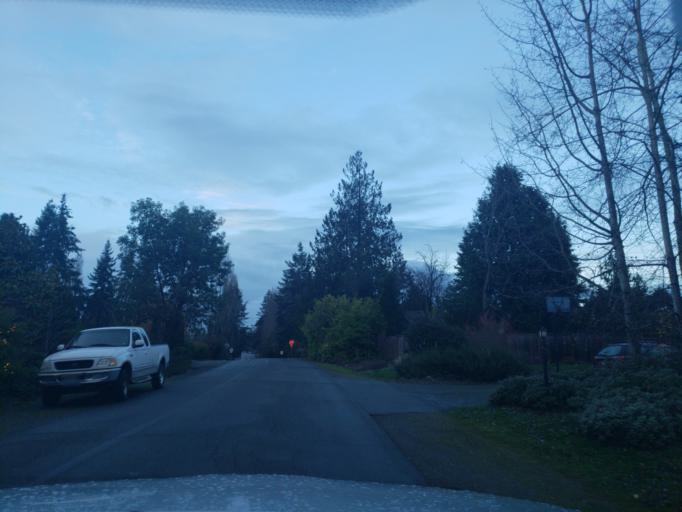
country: US
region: Washington
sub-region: Snohomish County
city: Woodway
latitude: 47.7649
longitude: -122.3772
